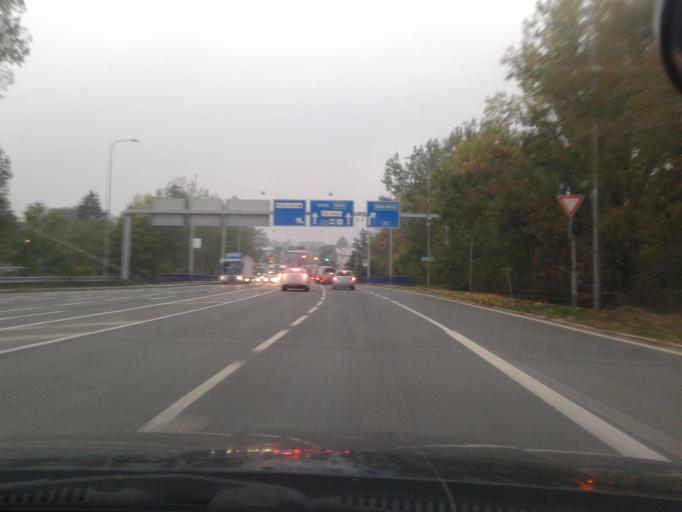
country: CZ
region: Moravskoslezsky
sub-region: Okres Ostrava-Mesto
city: Ostrava
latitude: 49.8071
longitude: 18.2768
